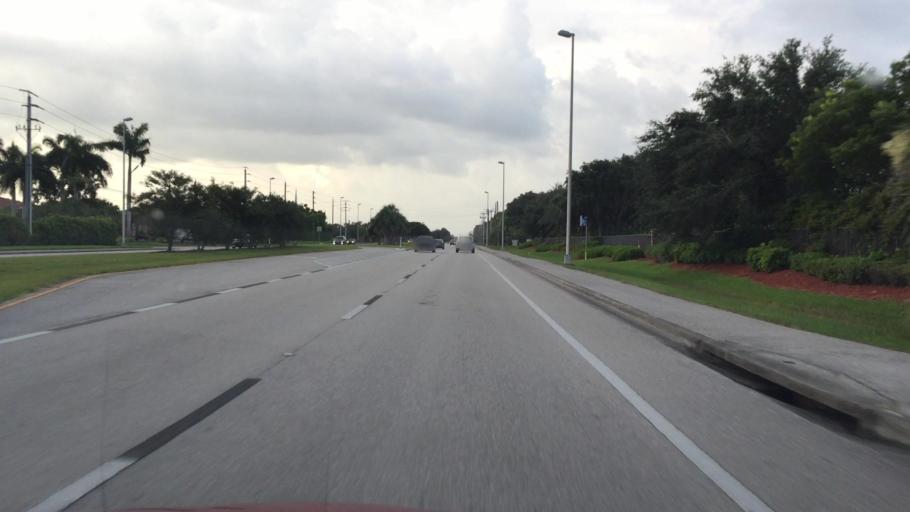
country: US
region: Florida
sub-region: Lee County
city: Estero
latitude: 26.4442
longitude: -81.7889
